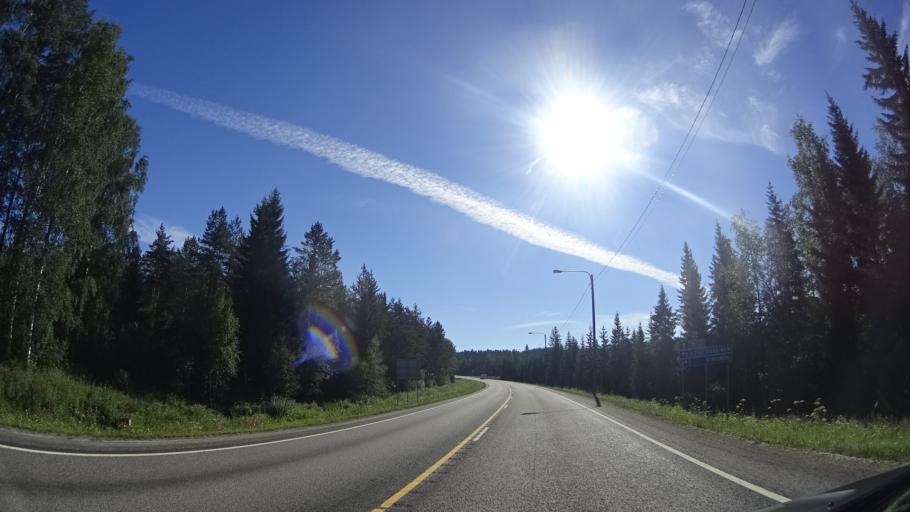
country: FI
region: Central Finland
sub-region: Jyvaeskylae
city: Petaejaevesi
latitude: 62.2704
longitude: 25.3332
